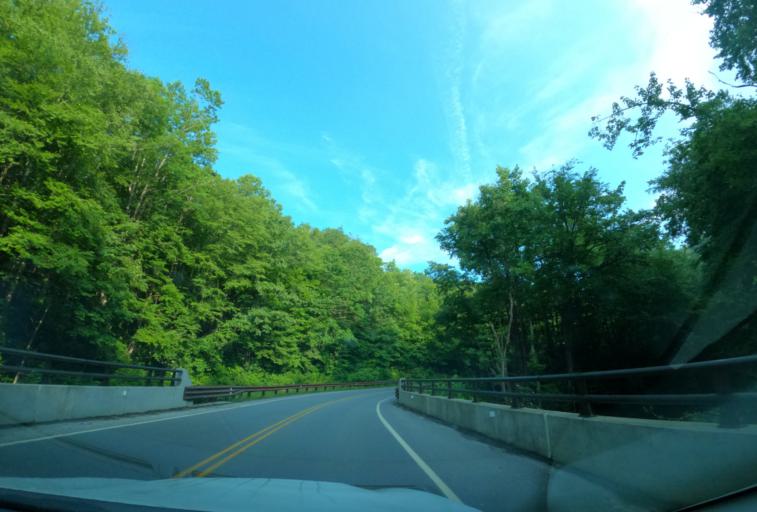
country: US
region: North Carolina
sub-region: Transylvania County
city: Brevard
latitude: 35.2479
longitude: -82.8883
